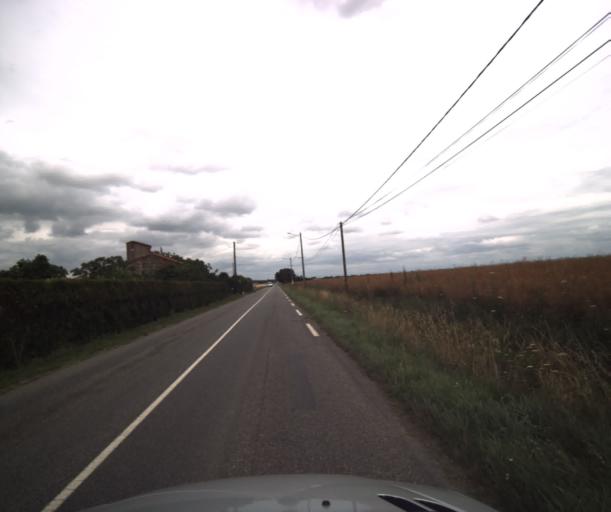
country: FR
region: Midi-Pyrenees
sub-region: Departement de la Haute-Garonne
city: Labarthe-sur-Leze
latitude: 43.4482
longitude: 1.4100
